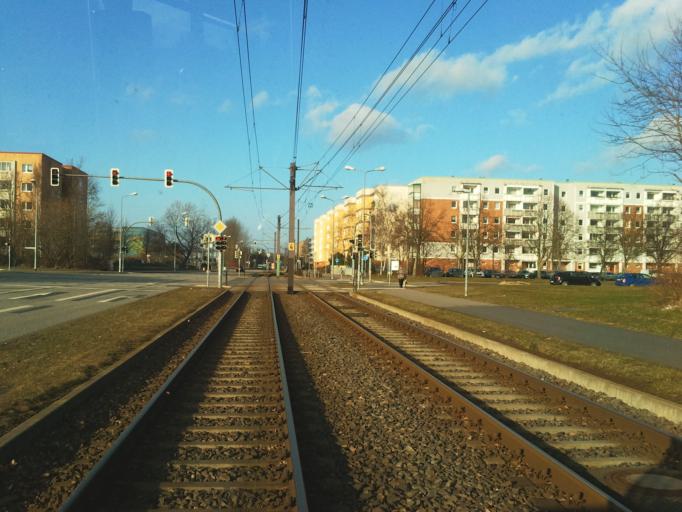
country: DE
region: Mecklenburg-Vorpommern
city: Warnemuende
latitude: 54.1534
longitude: 12.0592
